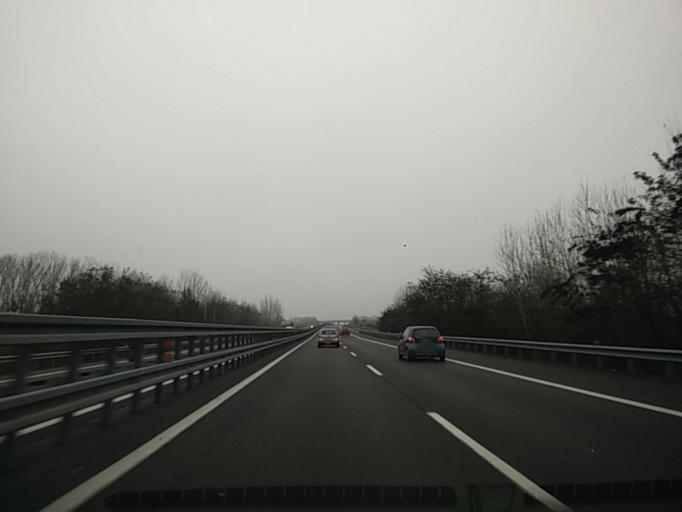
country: IT
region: Piedmont
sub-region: Provincia di Alessandria
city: Felizzano
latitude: 44.9163
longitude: 8.4411
